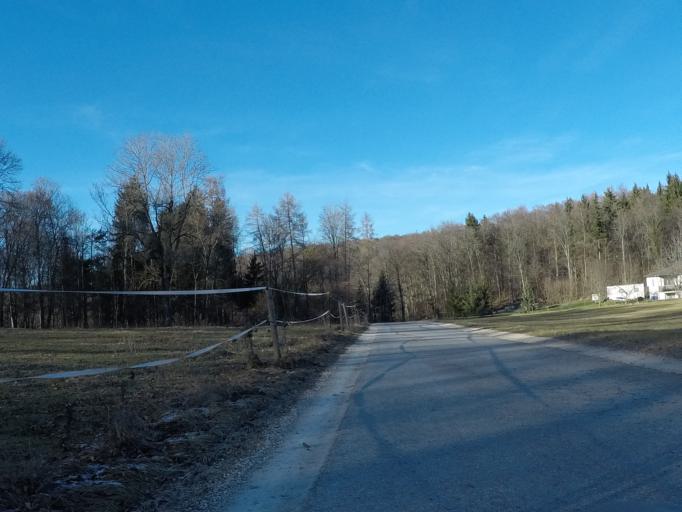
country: DE
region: Baden-Wuerttemberg
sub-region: Tuebingen Region
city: Sankt Johann
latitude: 48.4479
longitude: 9.3012
